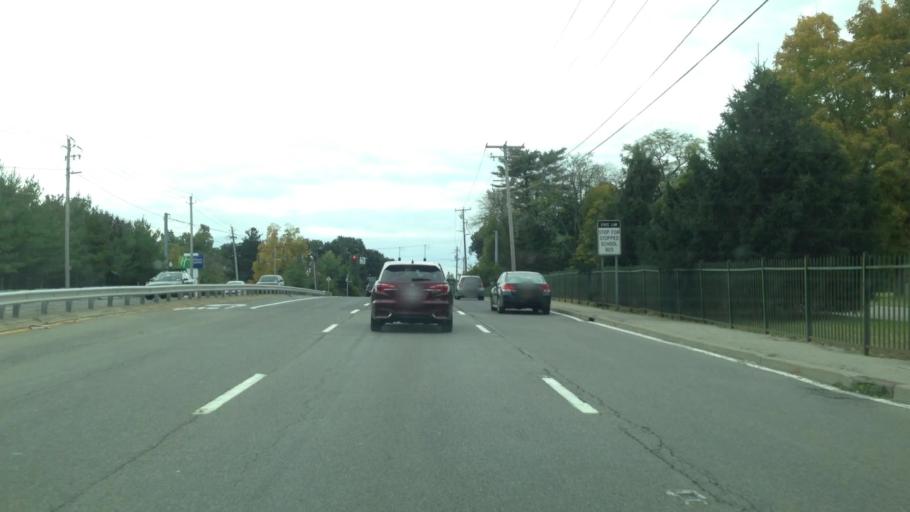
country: US
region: New York
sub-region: Dutchess County
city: Poughkeepsie
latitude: 41.6789
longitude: -73.9293
